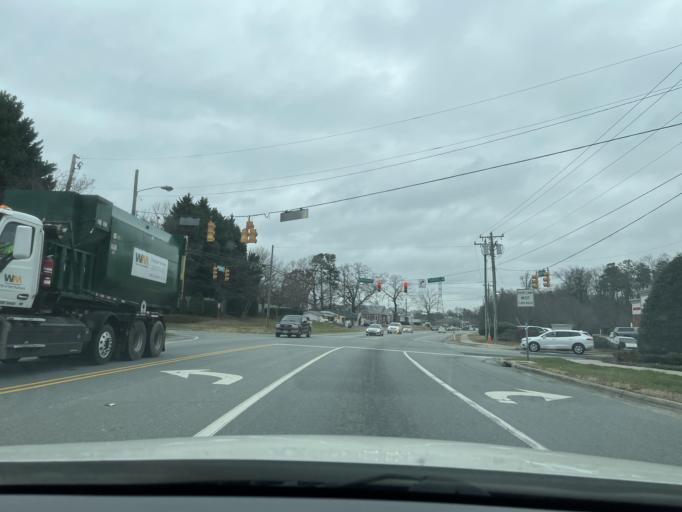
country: US
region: North Carolina
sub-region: Guilford County
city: Pleasant Garden
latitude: 36.0030
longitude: -79.8063
